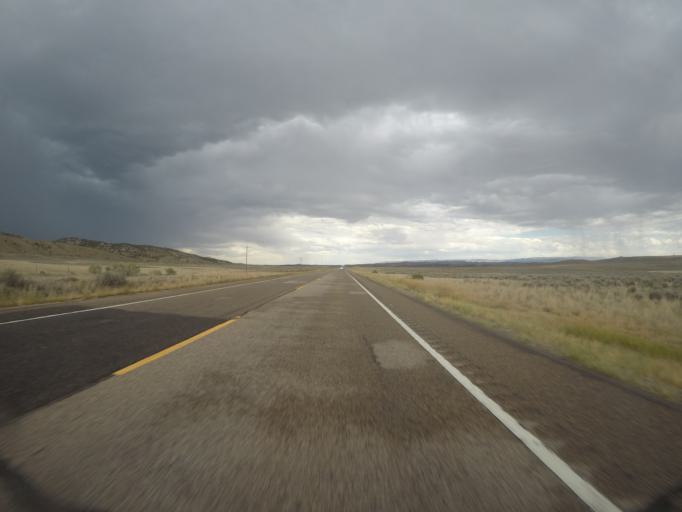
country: US
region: Colorado
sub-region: Rio Blanco County
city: Rangely
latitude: 40.2405
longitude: -108.9296
